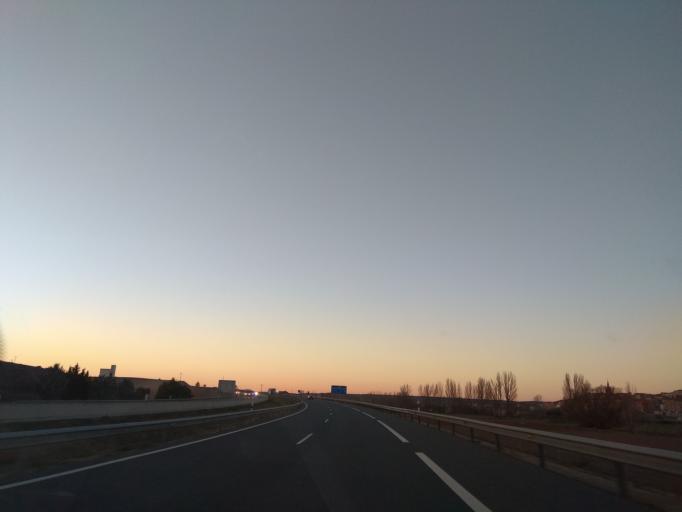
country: ES
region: Castille and Leon
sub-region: Provincia de Burgos
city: Lerma
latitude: 42.0169
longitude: -3.7559
